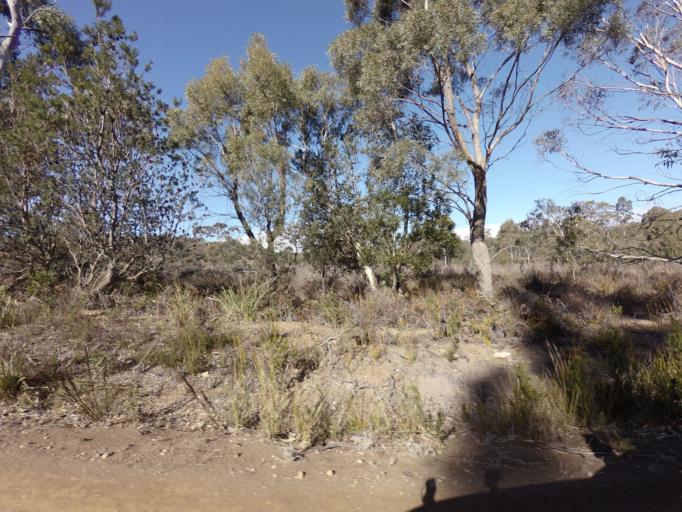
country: AU
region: Tasmania
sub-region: Sorell
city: Sorell
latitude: -42.3560
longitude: 147.9651
